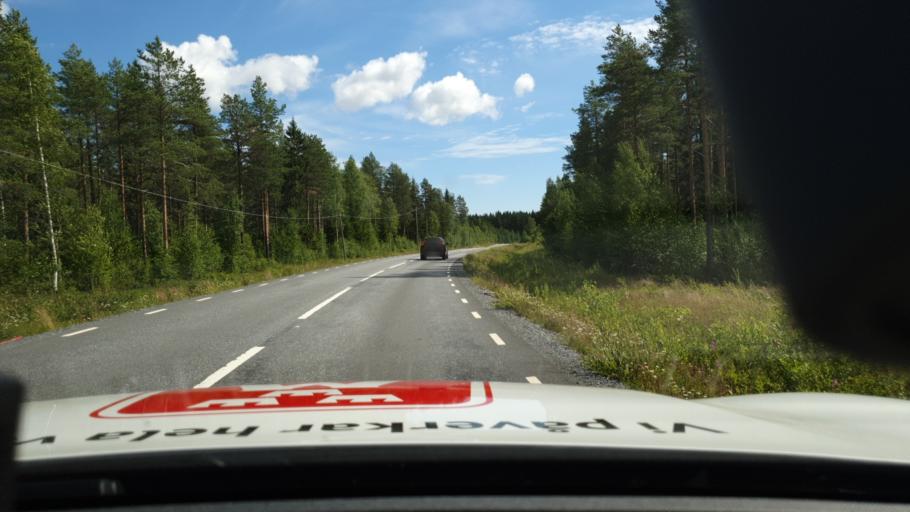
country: SE
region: Norrbotten
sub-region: Lulea Kommun
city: Ranea
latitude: 65.7900
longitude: 22.1434
